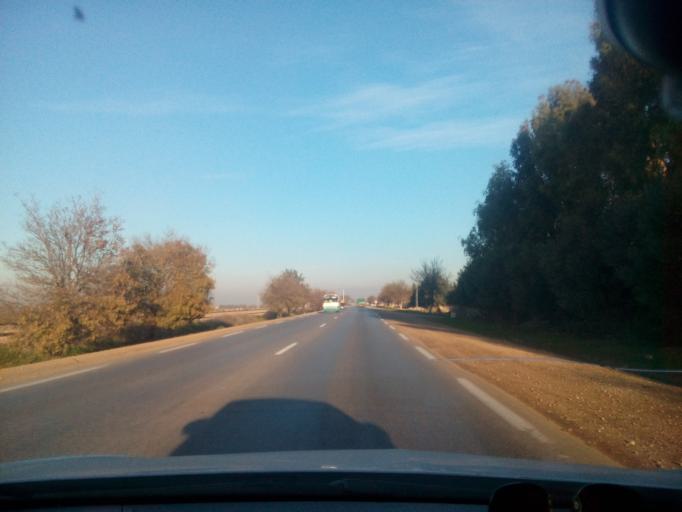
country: DZ
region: Chlef
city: Boukadir
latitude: 36.0476
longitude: 1.0852
